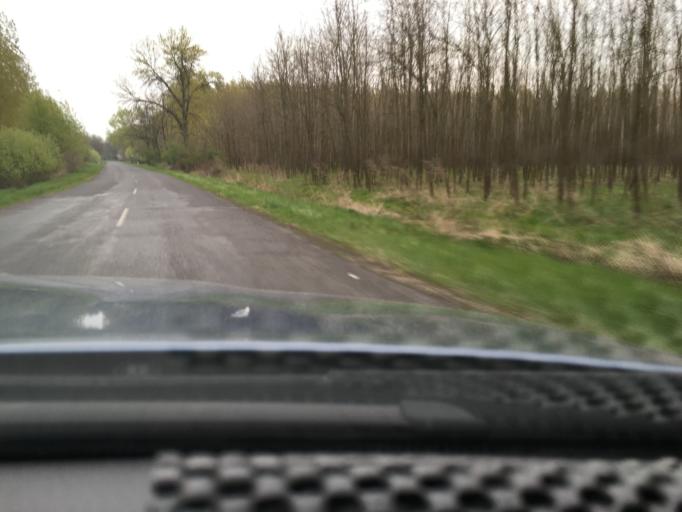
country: HU
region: Szabolcs-Szatmar-Bereg
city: Nyirlugos
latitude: 47.6961
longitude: 22.0681
